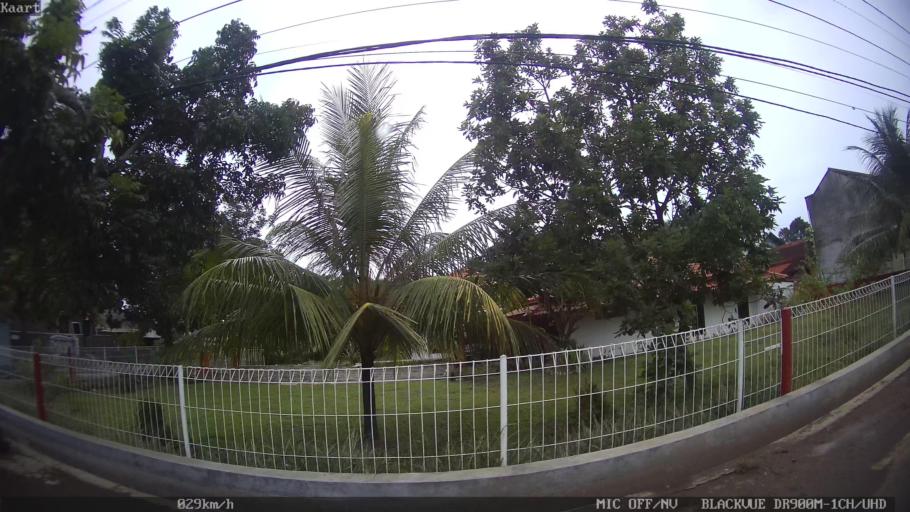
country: ID
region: Lampung
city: Kedaton
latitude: -5.3784
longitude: 105.2457
